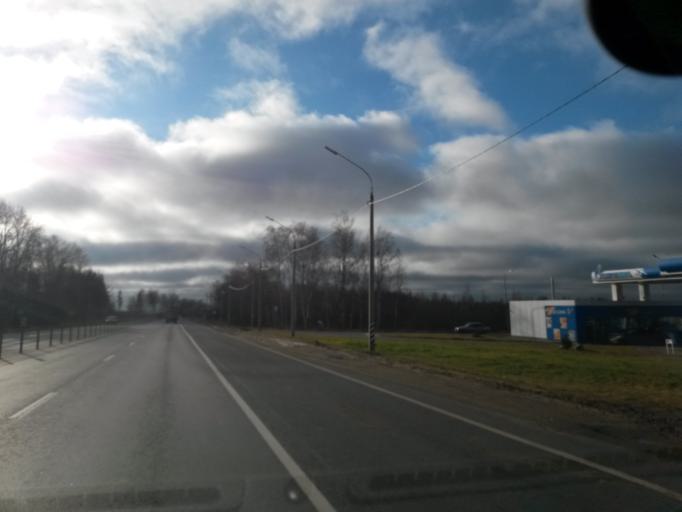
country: RU
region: Jaroslavl
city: Semibratovo
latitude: 57.3417
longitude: 39.5812
